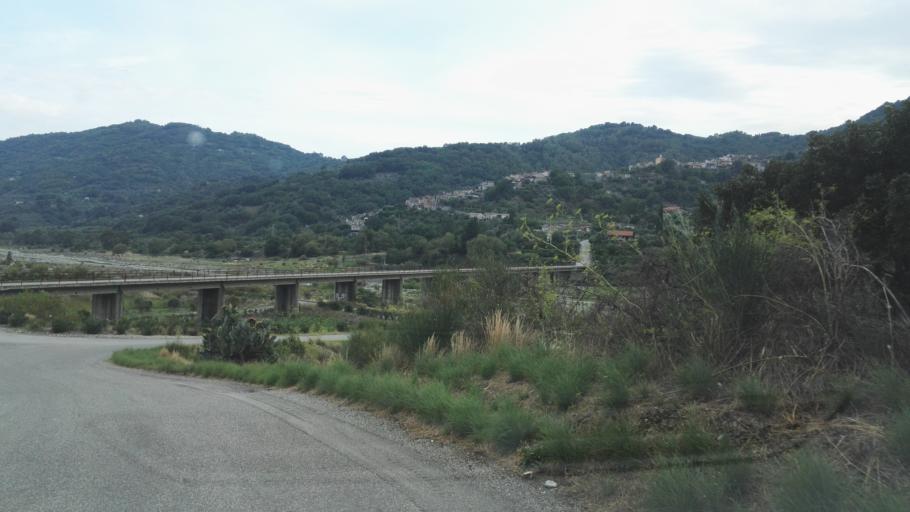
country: IT
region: Calabria
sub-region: Provincia di Reggio Calabria
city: Caulonia
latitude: 38.4205
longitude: 16.3785
